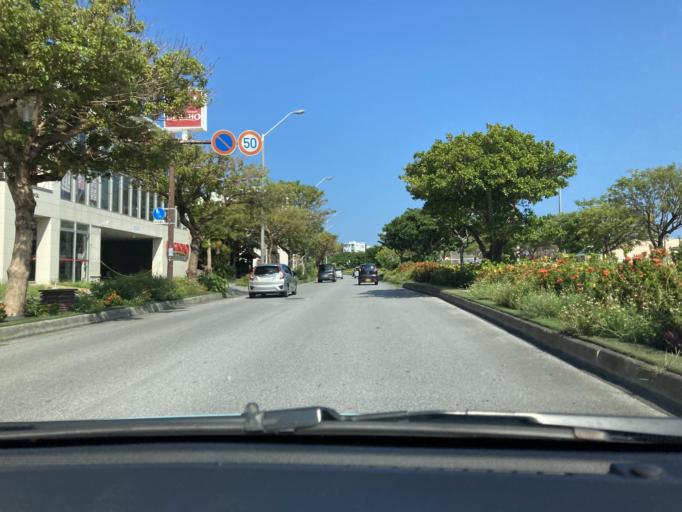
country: JP
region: Okinawa
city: Naha-shi
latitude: 26.2289
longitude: 127.6907
